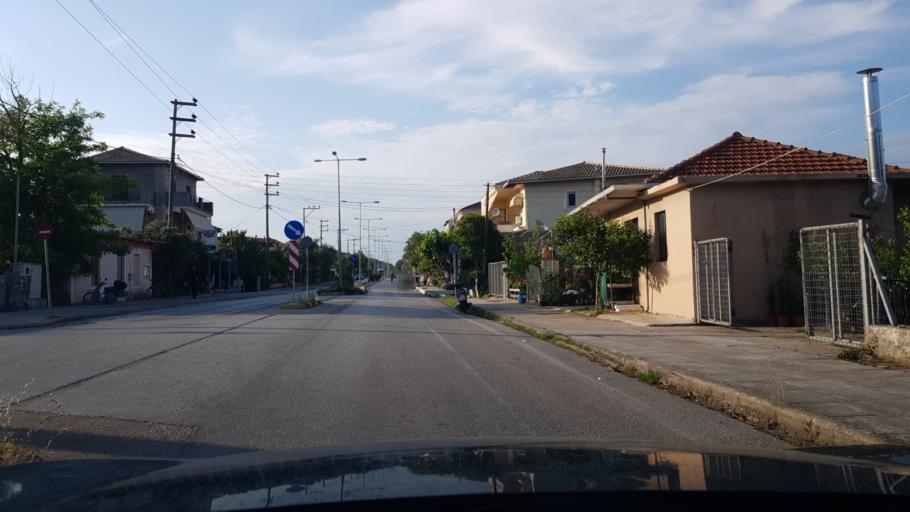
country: GR
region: Ionian Islands
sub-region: Lefkada
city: Lefkada
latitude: 38.7907
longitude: 20.7188
